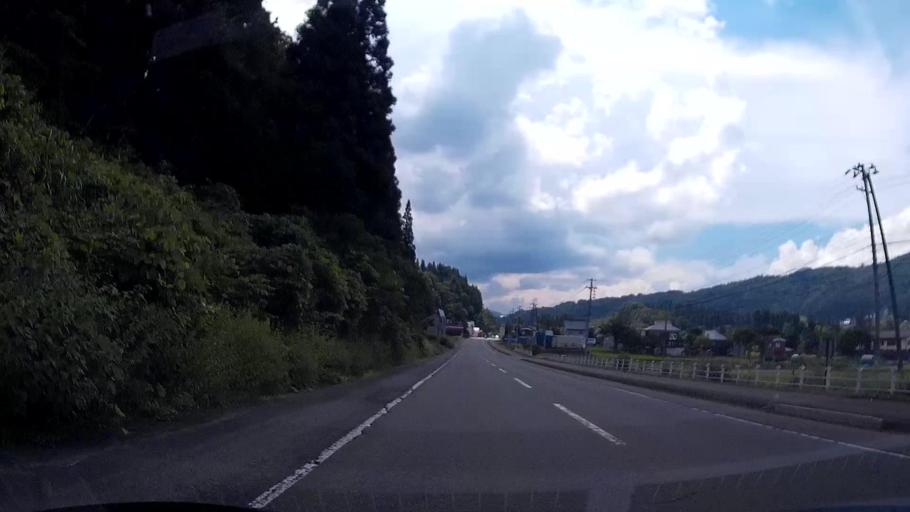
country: JP
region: Niigata
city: Tokamachi
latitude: 36.9956
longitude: 138.5988
